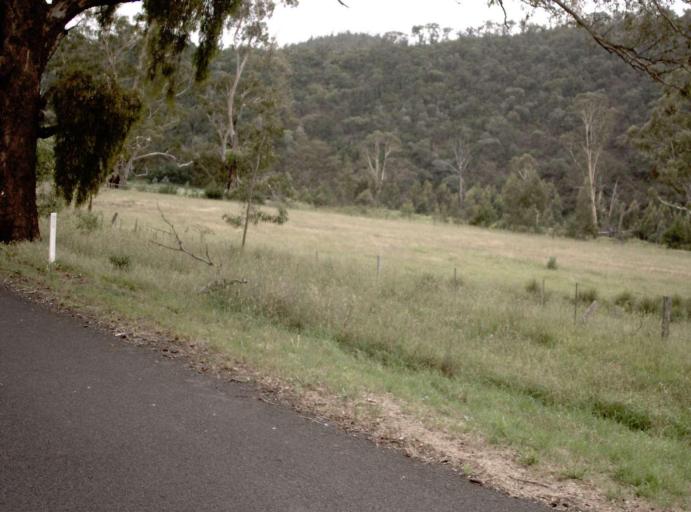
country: AU
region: Victoria
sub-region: Wellington
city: Heyfield
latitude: -37.7919
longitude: 146.6793
